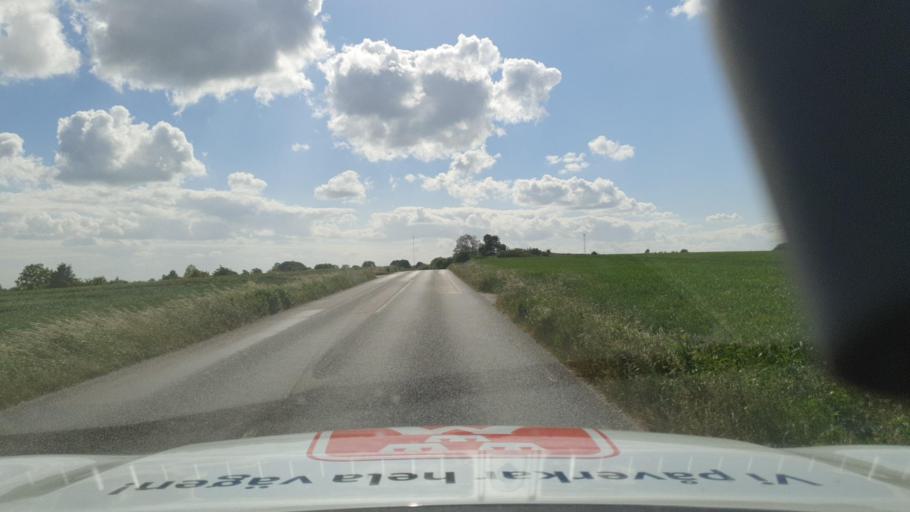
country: SE
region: Skane
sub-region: Simrishamns Kommun
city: Simrishamn
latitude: 55.5633
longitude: 14.2979
